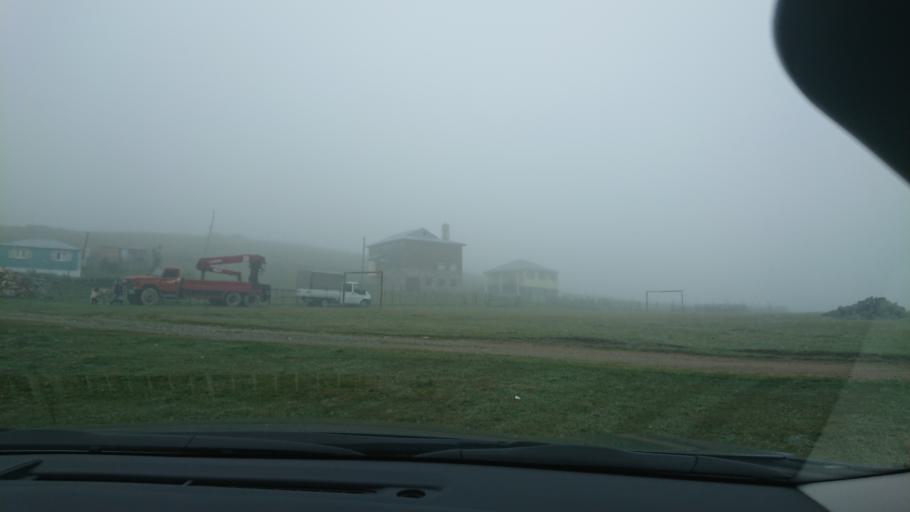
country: TR
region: Gumushane
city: Kurtun
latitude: 40.6730
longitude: 38.9937
